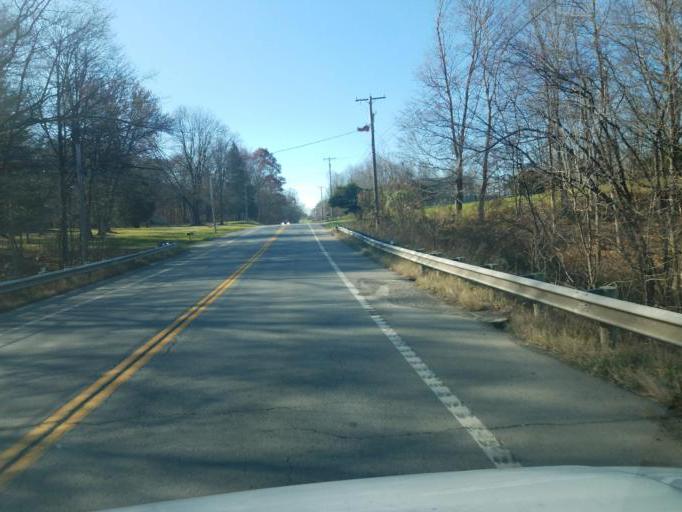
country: US
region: Ohio
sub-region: Ashland County
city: Ashland
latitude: 40.8269
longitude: -82.3836
